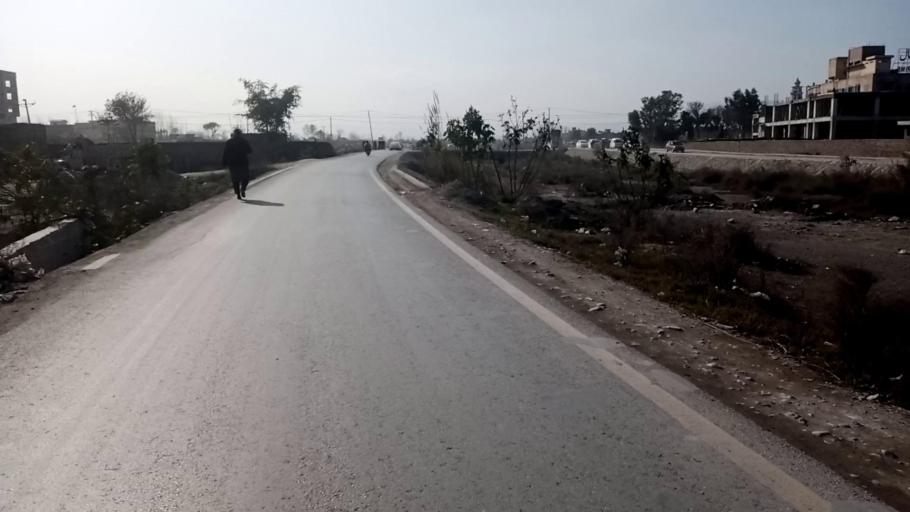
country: PK
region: Khyber Pakhtunkhwa
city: Peshawar
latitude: 34.0365
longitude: 71.5320
